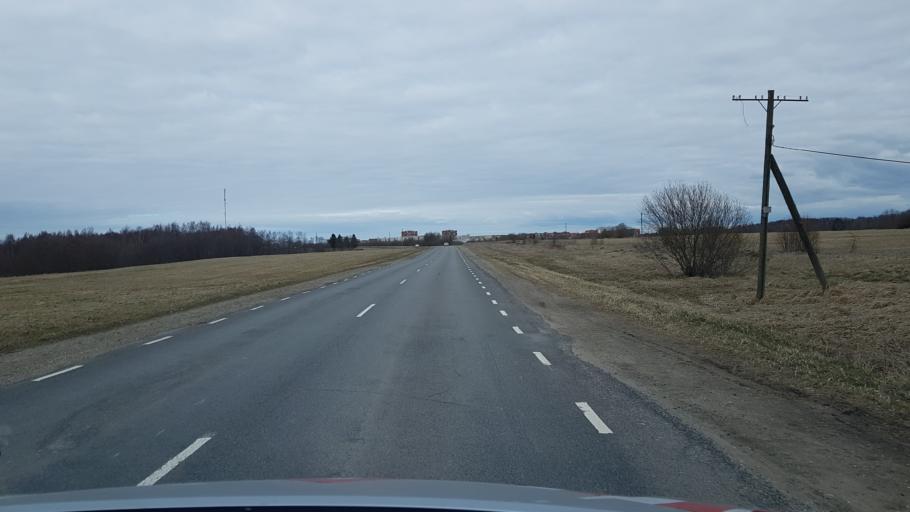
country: EE
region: Ida-Virumaa
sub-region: Sillamaee linn
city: Sillamae
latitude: 59.3827
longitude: 27.7679
